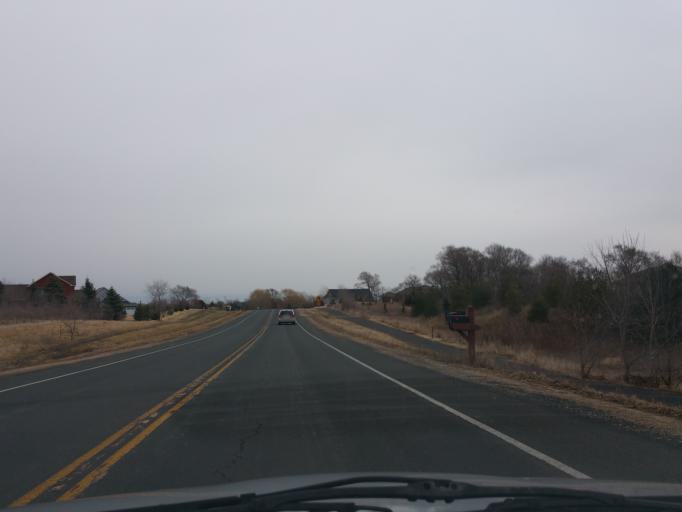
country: US
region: Wisconsin
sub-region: Saint Croix County
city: North Hudson
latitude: 44.9873
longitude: -92.7114
